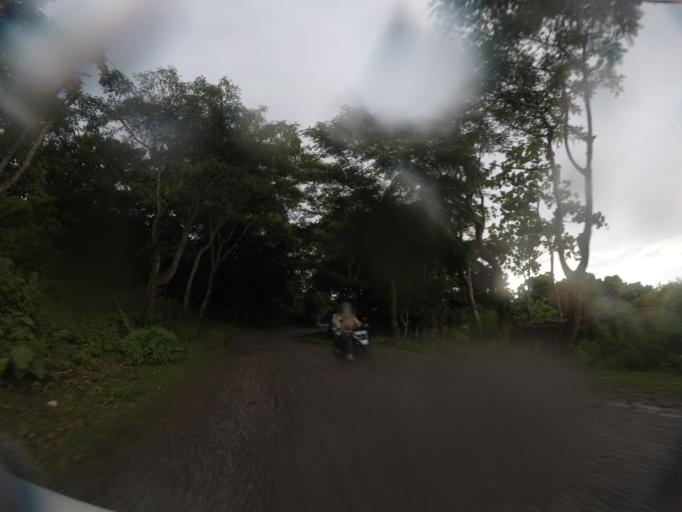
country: TL
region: Bobonaro
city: Maliana
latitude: -8.9620
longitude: 125.0305
